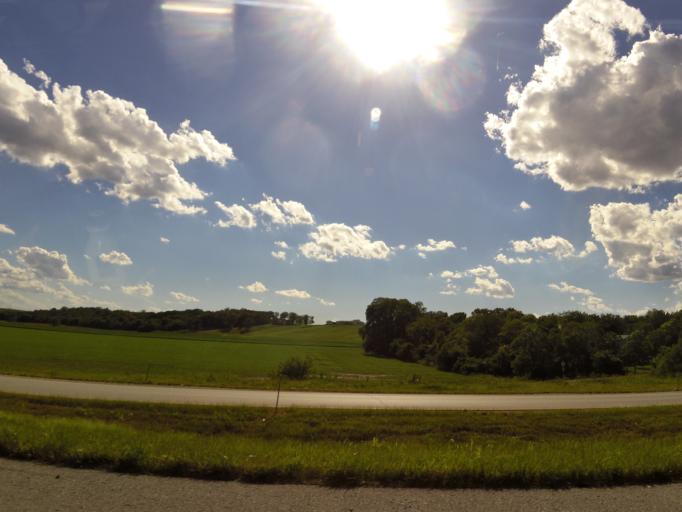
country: US
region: Illinois
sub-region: Adams County
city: Quincy
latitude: 40.0101
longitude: -91.5266
